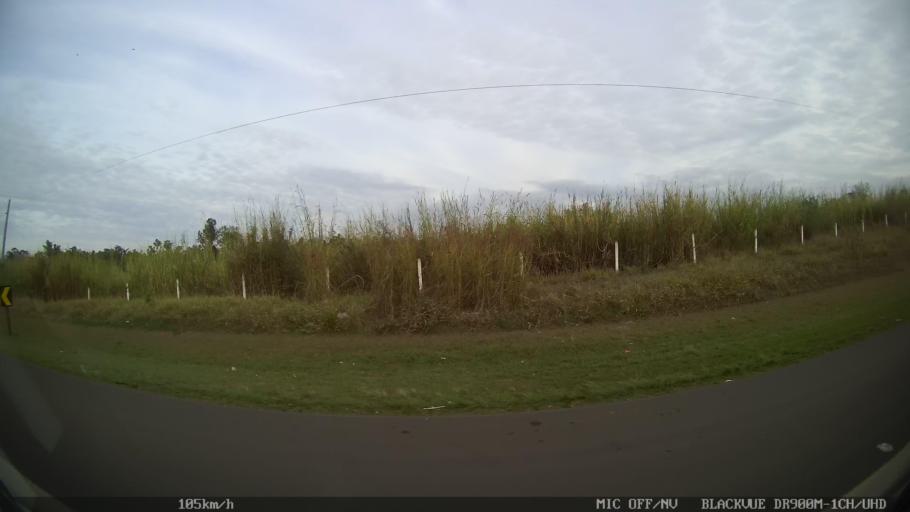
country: BR
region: Sao Paulo
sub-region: Piracicaba
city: Piracicaba
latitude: -22.7006
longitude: -47.5977
